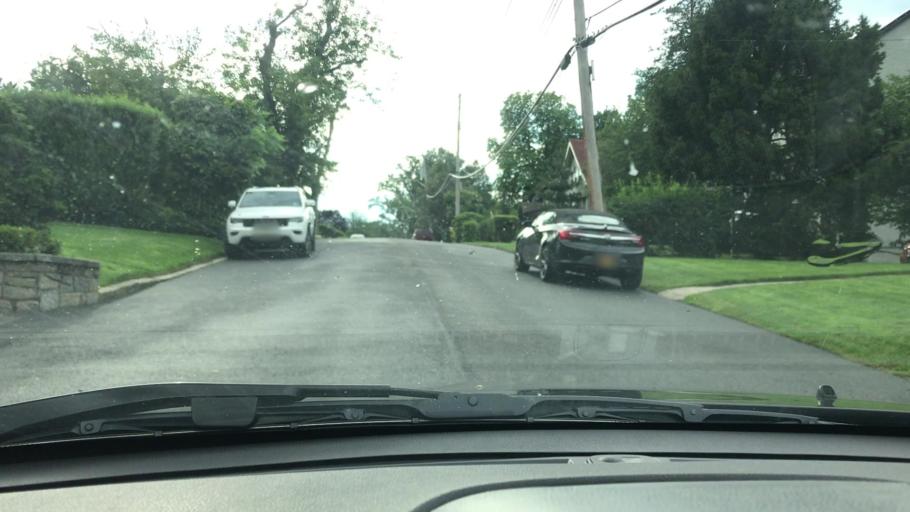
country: US
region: New York
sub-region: Westchester County
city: New Rochelle
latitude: 40.9349
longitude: -73.7934
